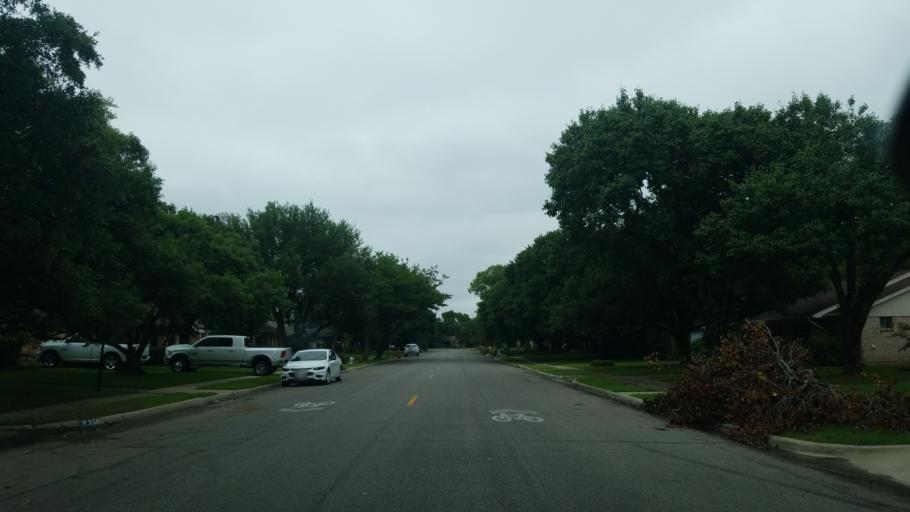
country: US
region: Texas
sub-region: Dallas County
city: Farmers Branch
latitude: 32.9018
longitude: -96.8659
